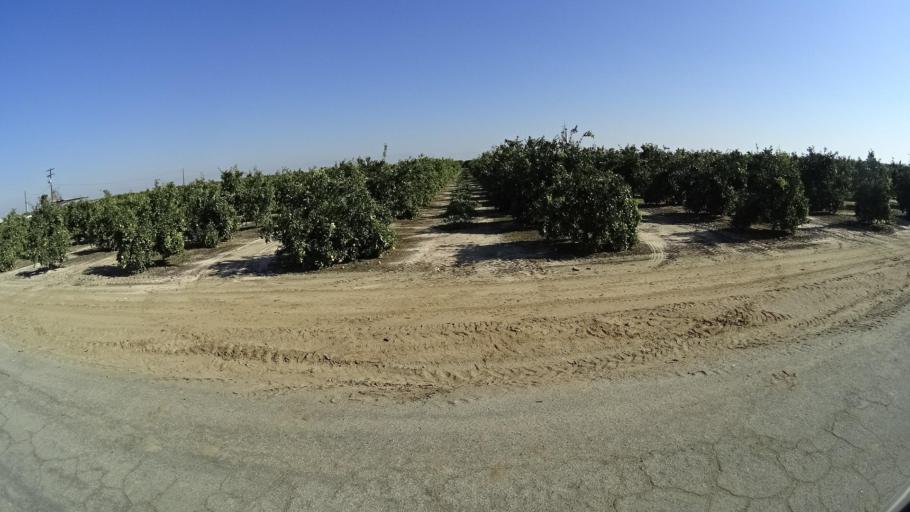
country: US
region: California
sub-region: Tulare County
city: Richgrove
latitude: 35.7246
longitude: -119.1429
